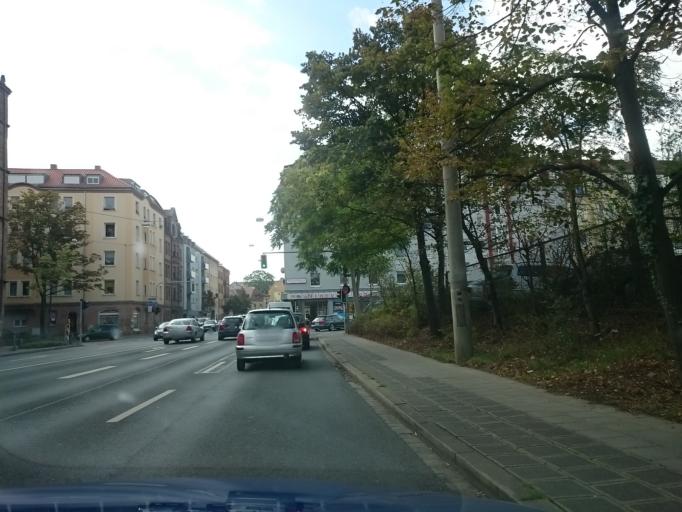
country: DE
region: Bavaria
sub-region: Regierungsbezirk Mittelfranken
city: Nuernberg
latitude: 49.4464
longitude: 11.0975
